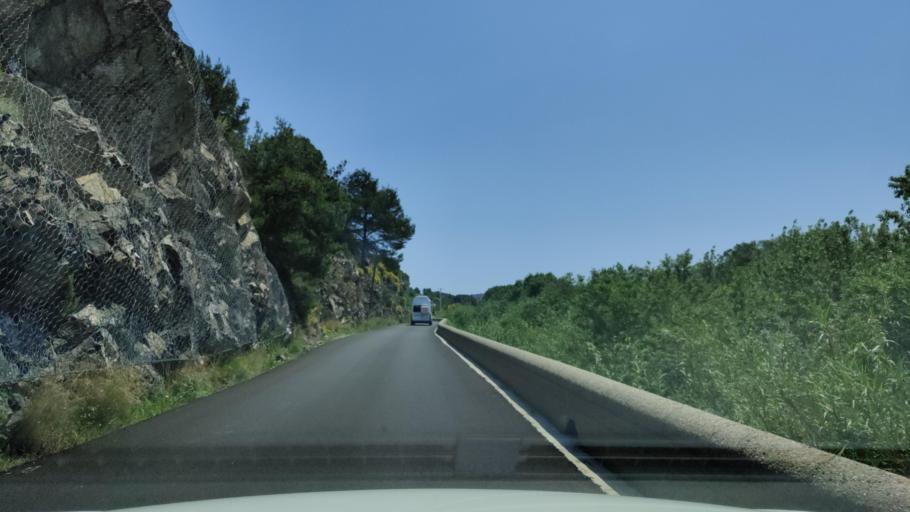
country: FR
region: Languedoc-Roussillon
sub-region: Departement des Pyrenees-Orientales
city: Baixas
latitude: 42.7847
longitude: 2.7742
